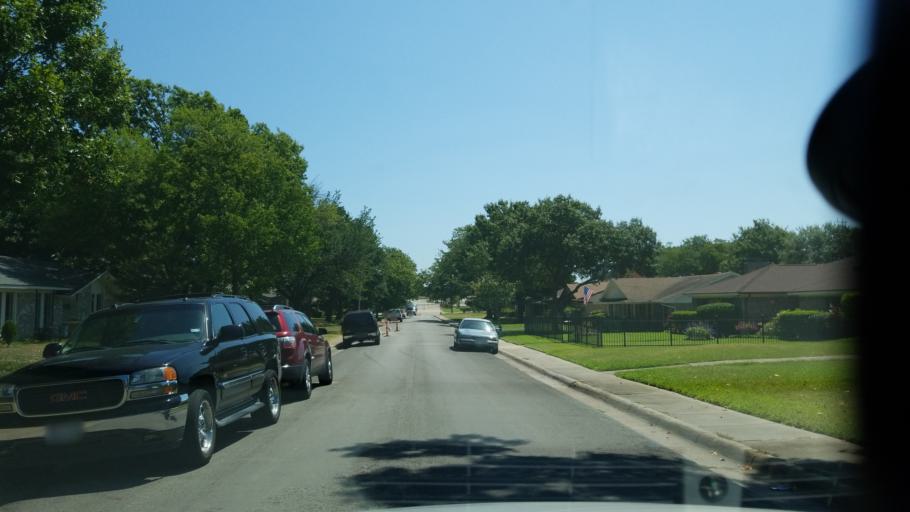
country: US
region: Texas
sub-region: Dallas County
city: Duncanville
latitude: 32.6532
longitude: -96.8934
